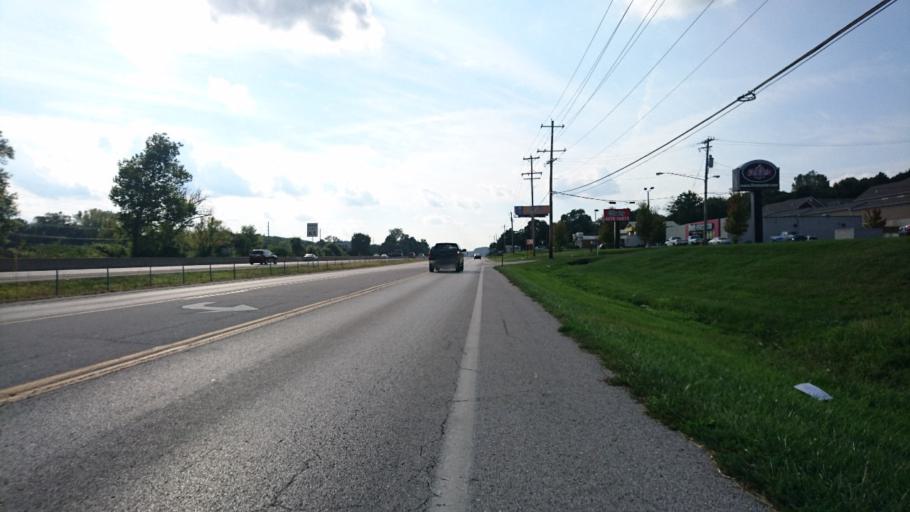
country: US
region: Missouri
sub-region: Saint Louis County
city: Eureka
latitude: 38.5043
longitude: -90.6477
